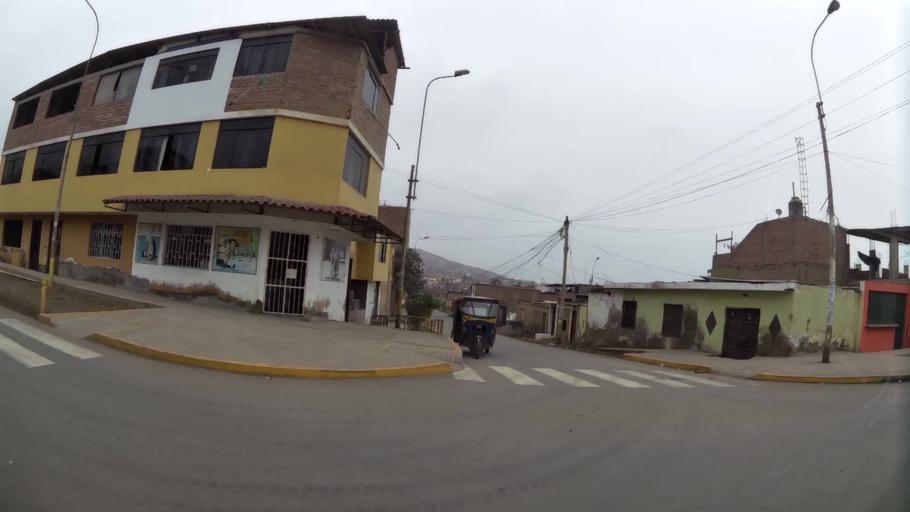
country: PE
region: Lima
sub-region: Lima
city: Surco
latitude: -12.2181
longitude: -76.9098
